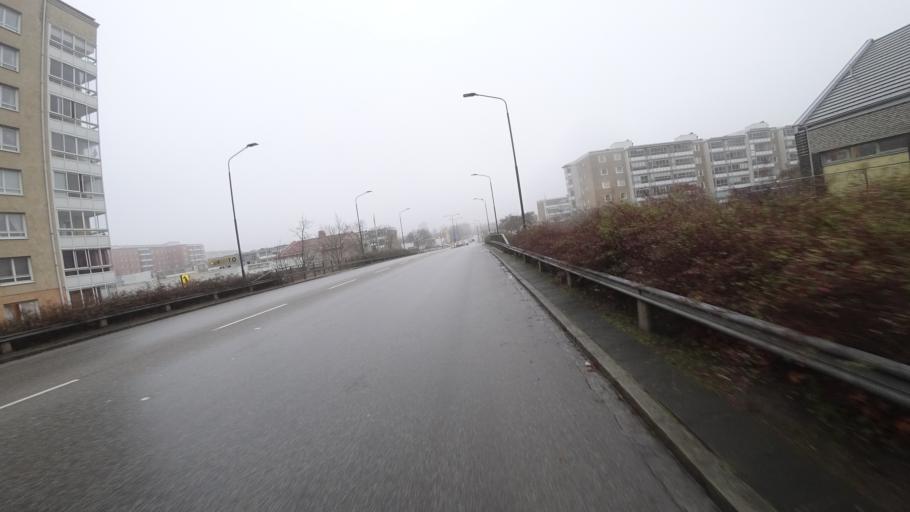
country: SE
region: Skane
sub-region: Malmo
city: Malmoe
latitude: 55.5669
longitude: 13.0112
